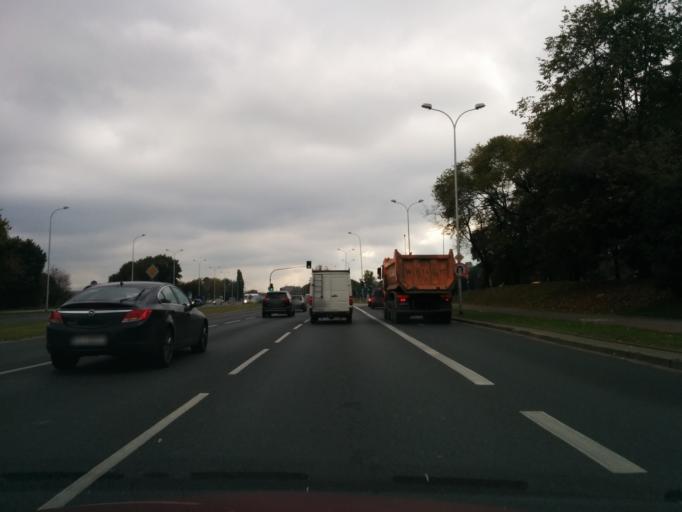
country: PL
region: Masovian Voivodeship
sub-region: Warszawa
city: Praga Polnoc
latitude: 52.2570
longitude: 21.0096
